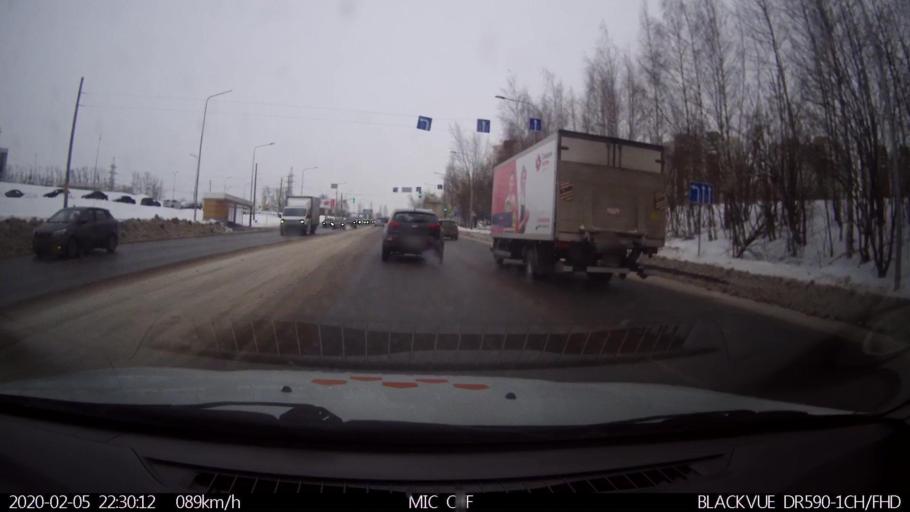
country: RU
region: Nizjnij Novgorod
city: Imeni Stepana Razina
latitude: 54.7442
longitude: 44.1567
